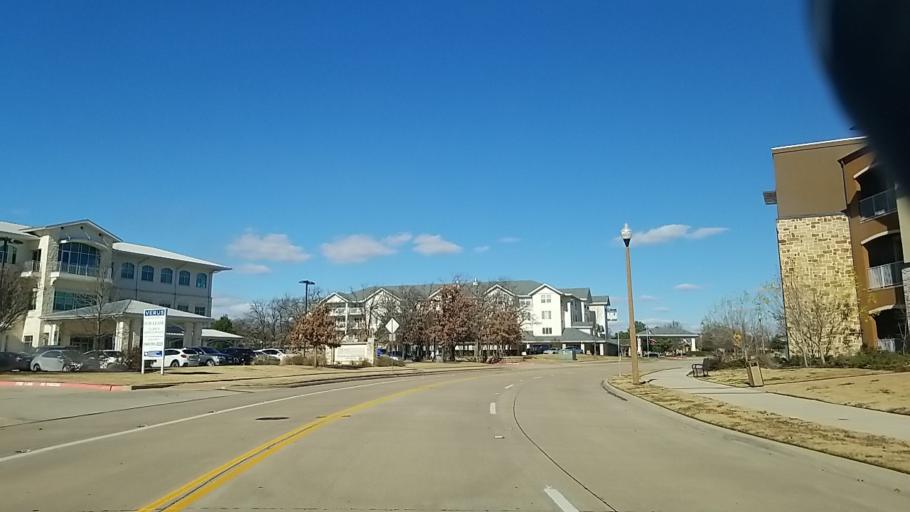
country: US
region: Texas
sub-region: Denton County
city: Corinth
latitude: 33.1738
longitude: -97.0999
